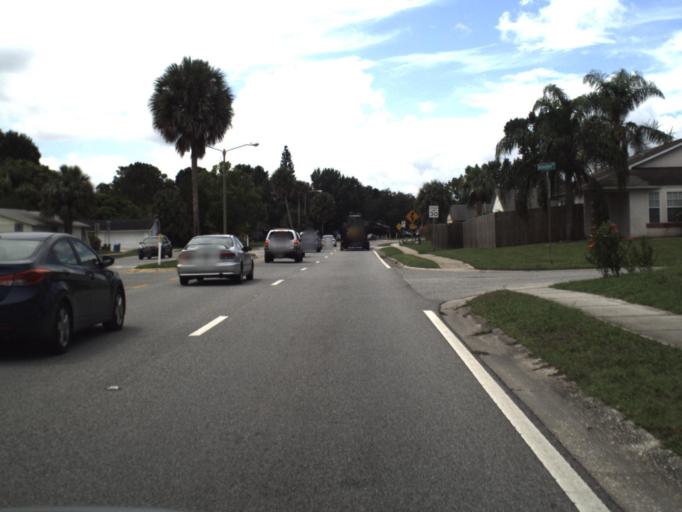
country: US
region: Florida
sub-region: Pasco County
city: Elfers
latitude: 28.2140
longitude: -82.6928
